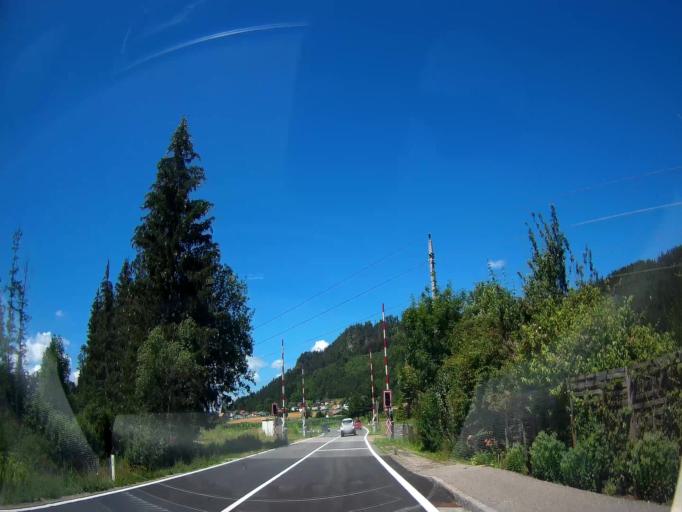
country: AT
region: Carinthia
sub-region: Politischer Bezirk Sankt Veit an der Glan
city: St. Georgen am Laengsee
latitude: 46.7648
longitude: 14.4462
